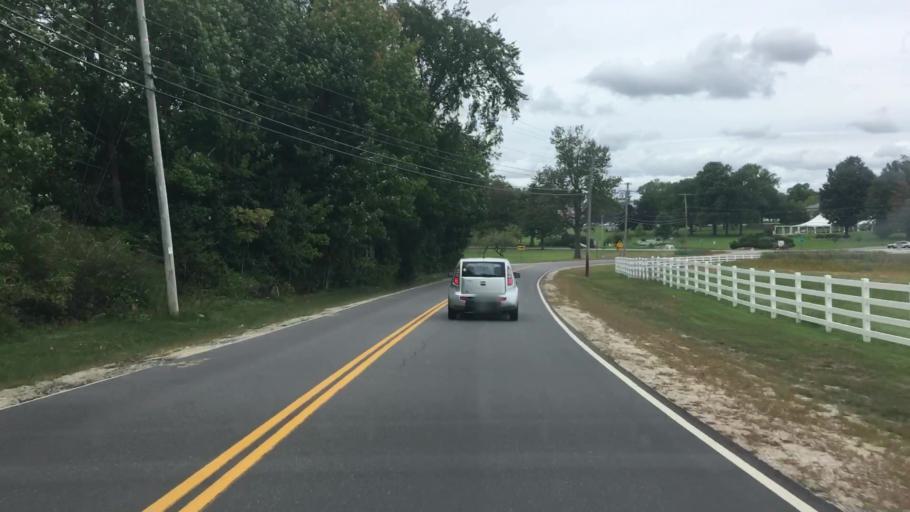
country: US
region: Maine
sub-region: Cumberland County
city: New Gloucester
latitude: 43.8982
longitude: -70.2565
